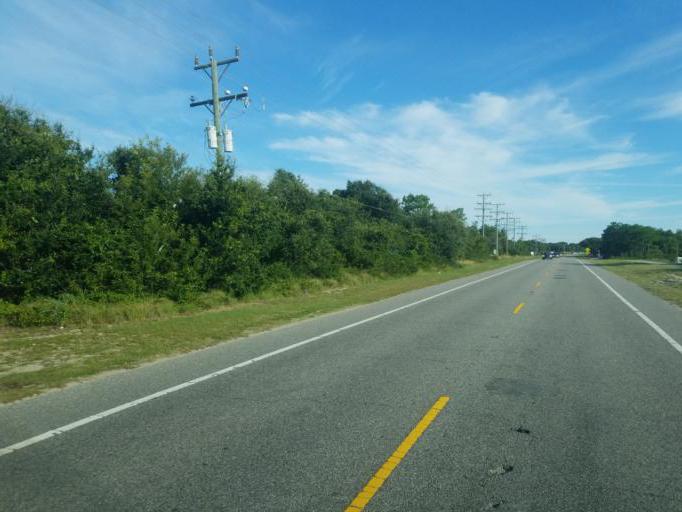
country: US
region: North Carolina
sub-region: Dare County
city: Southern Shores
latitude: 36.3218
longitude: -75.8158
